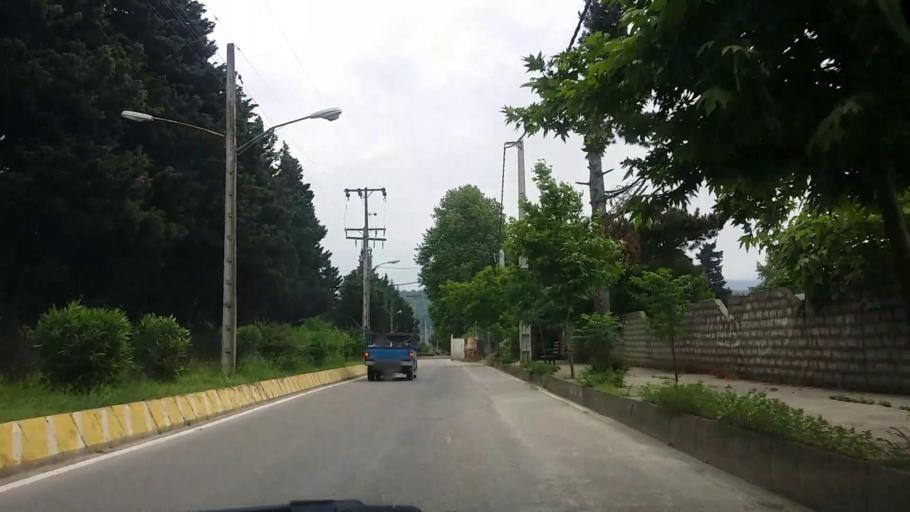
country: IR
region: Mazandaran
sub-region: Nowshahr
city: Nowshahr
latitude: 36.6302
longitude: 51.5026
